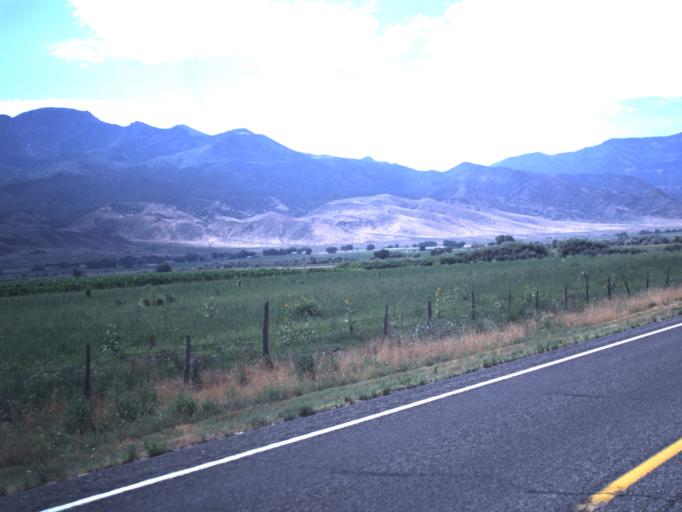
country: US
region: Utah
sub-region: Sevier County
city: Monroe
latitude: 38.6856
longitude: -112.1217
